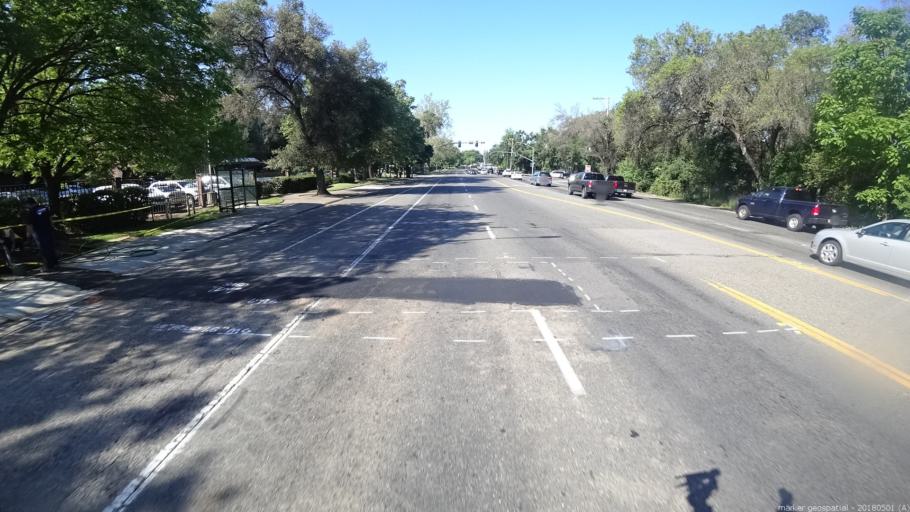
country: US
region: California
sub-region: Sacramento County
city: Foothill Farms
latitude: 38.6442
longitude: -121.3646
